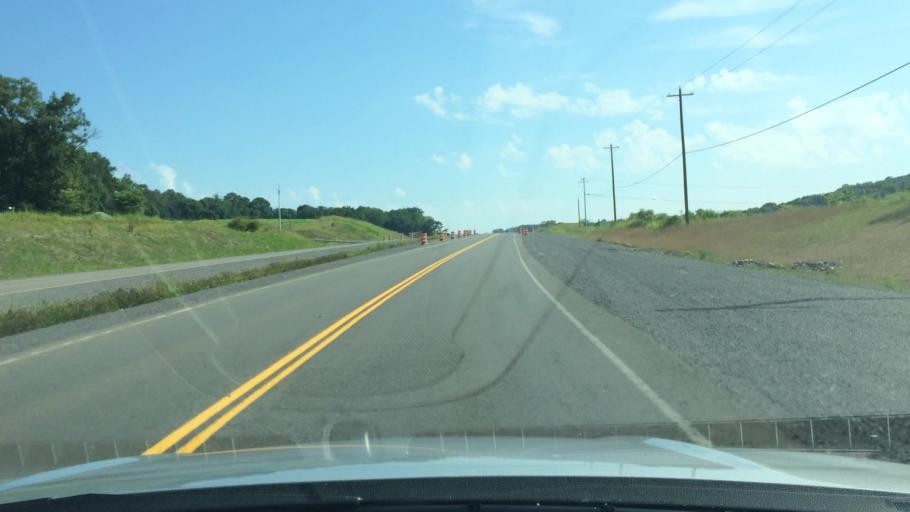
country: US
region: Tennessee
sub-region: Jefferson County
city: White Pine
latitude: 36.1152
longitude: -83.3412
